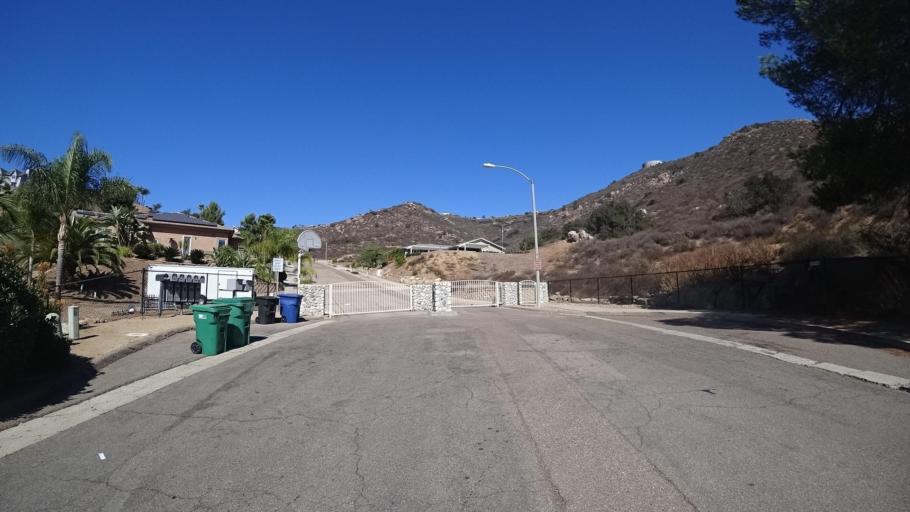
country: US
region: California
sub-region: San Diego County
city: Winter Gardens
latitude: 32.8277
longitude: -116.9476
